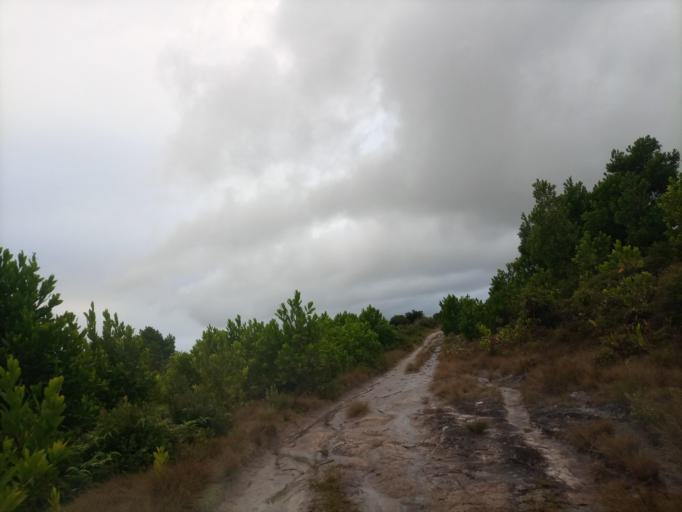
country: MG
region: Anosy
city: Fort Dauphin
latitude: -24.6477
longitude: 47.2063
